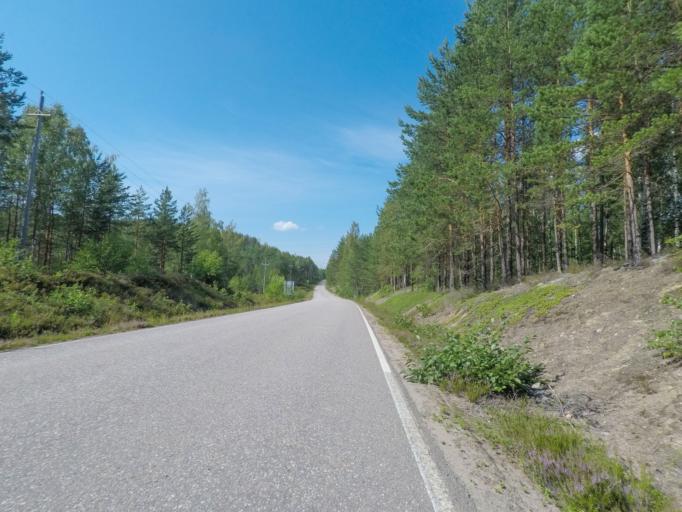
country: FI
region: Southern Savonia
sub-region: Mikkeli
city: Puumala
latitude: 61.4616
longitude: 28.1750
